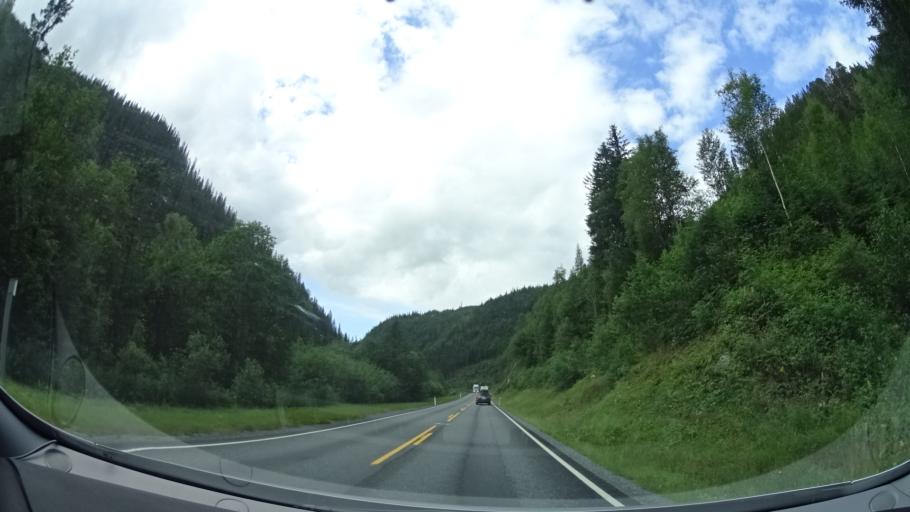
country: NO
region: Nord-Trondelag
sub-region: Meraker
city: Meraker
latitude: 63.4571
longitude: 11.5516
